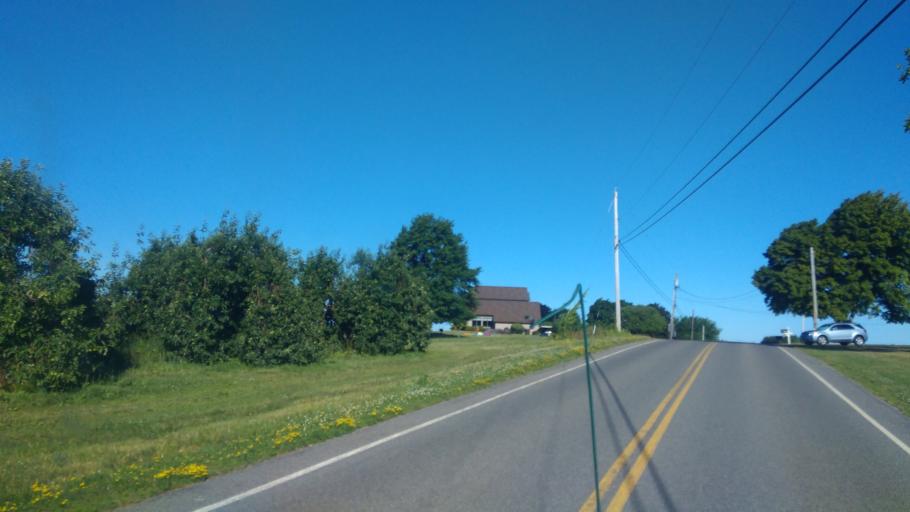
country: US
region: New York
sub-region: Wayne County
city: Williamson
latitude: 43.2812
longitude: -77.1301
